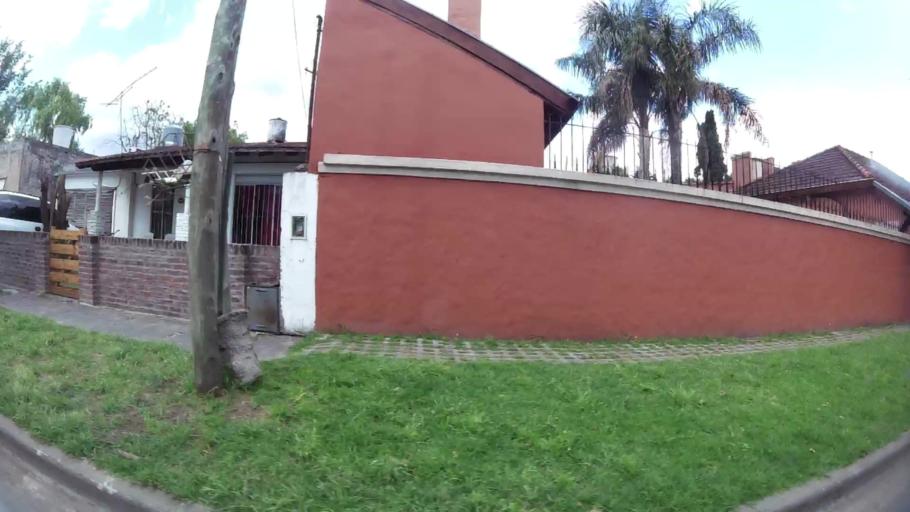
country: AR
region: Buenos Aires
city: Ituzaingo
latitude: -34.6394
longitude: -58.6713
